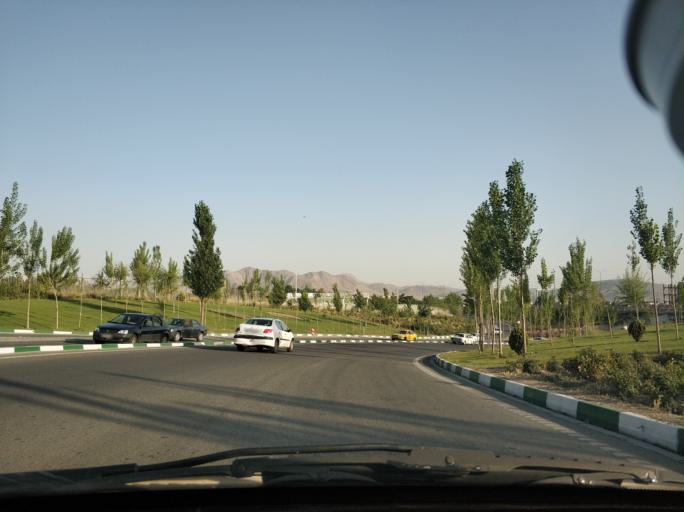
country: IR
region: Tehran
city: Tajrish
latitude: 35.7547
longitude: 51.5782
